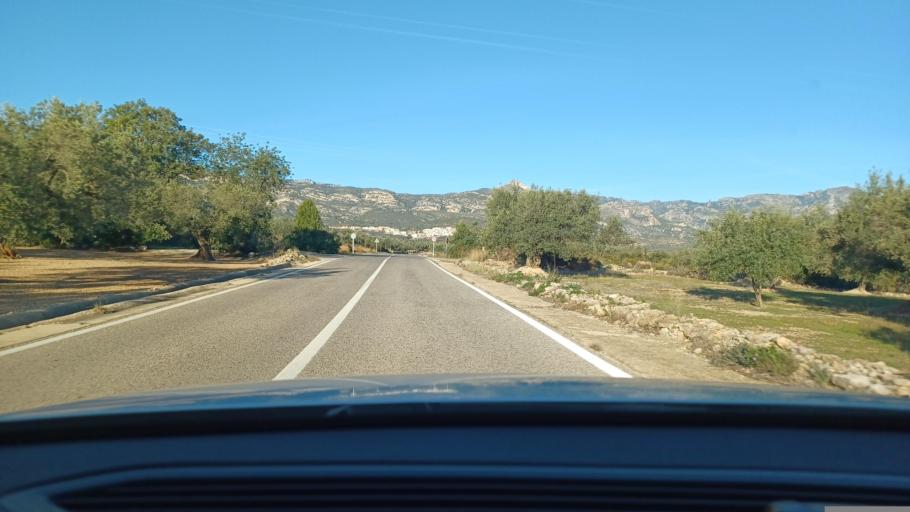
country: ES
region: Catalonia
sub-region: Provincia de Tarragona
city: Mas de Barberans
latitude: 40.7229
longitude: 0.3944
